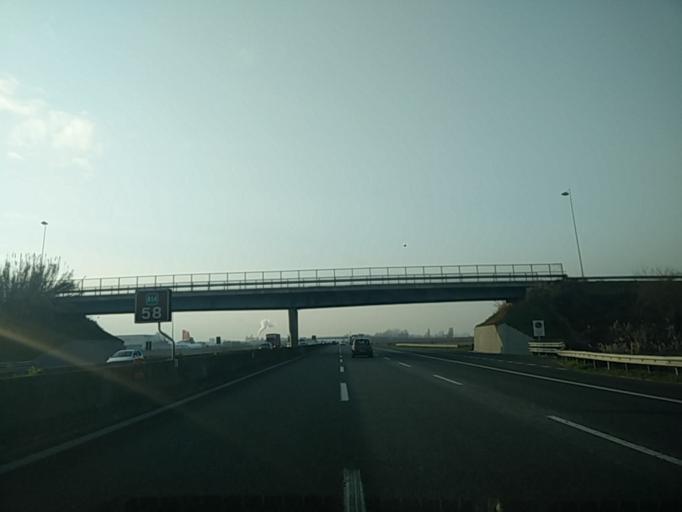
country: IT
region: Emilia-Romagna
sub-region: Provincia di Ravenna
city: Solarolo
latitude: 44.3322
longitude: 11.8839
